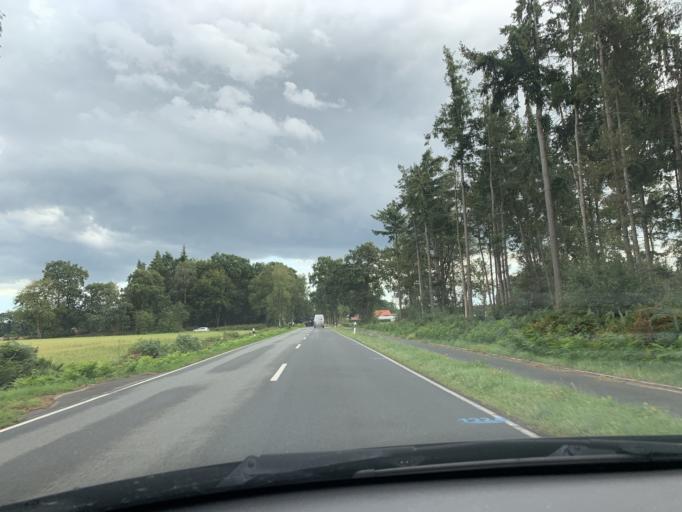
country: DE
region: Lower Saxony
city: Westerstede
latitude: 53.2996
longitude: 7.9168
